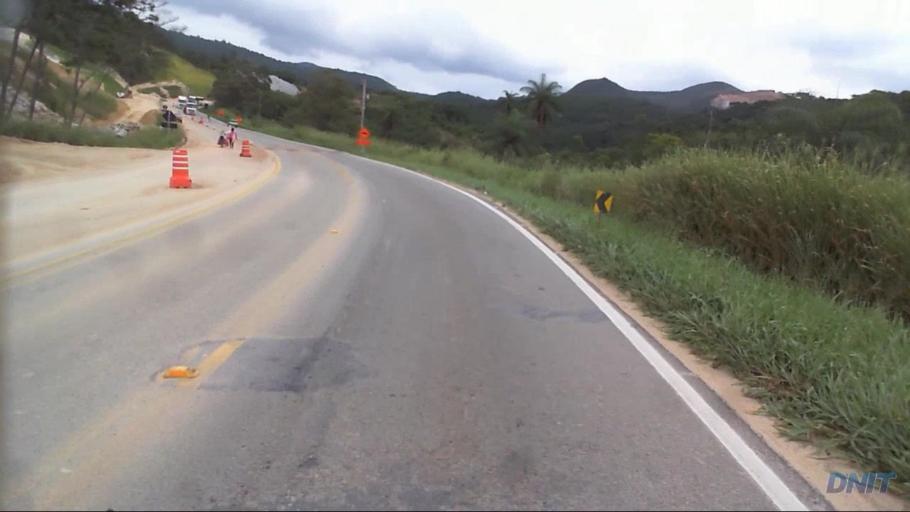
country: BR
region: Minas Gerais
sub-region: Caete
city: Caete
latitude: -19.7835
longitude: -43.6675
